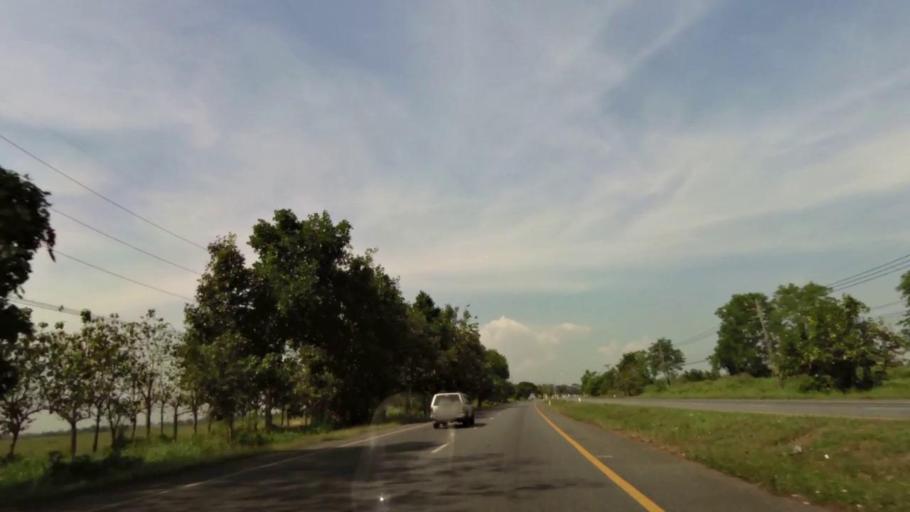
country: TH
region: Uttaradit
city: Tron
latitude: 17.5599
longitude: 100.1639
